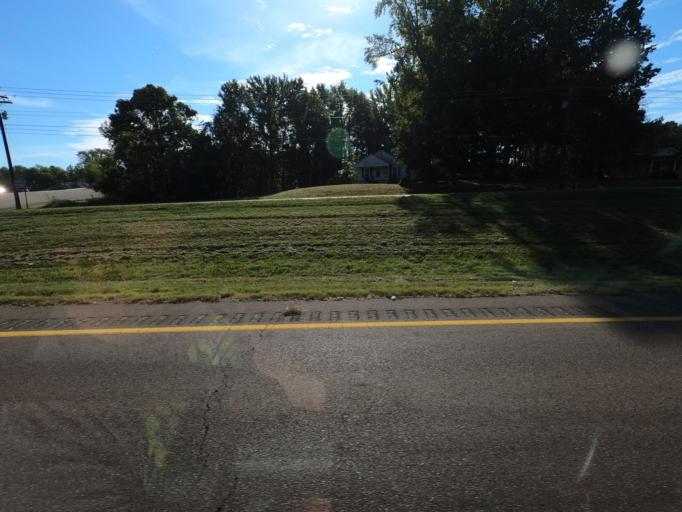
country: US
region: Tennessee
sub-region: Tipton County
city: Brighton
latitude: 35.4715
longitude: -89.7510
